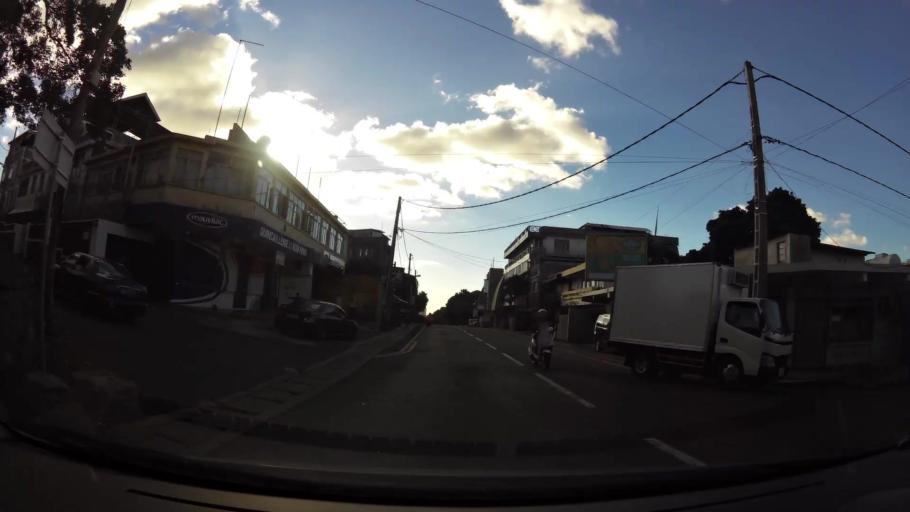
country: MU
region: Plaines Wilhems
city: Ebene
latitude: -20.2347
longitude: 57.4707
